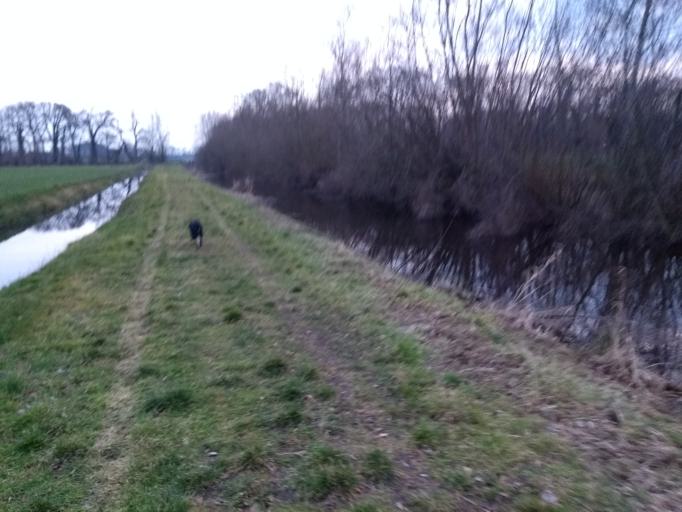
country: NL
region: Overijssel
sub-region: Gemeente Borne
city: Borne
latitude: 52.3288
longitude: 6.7452
